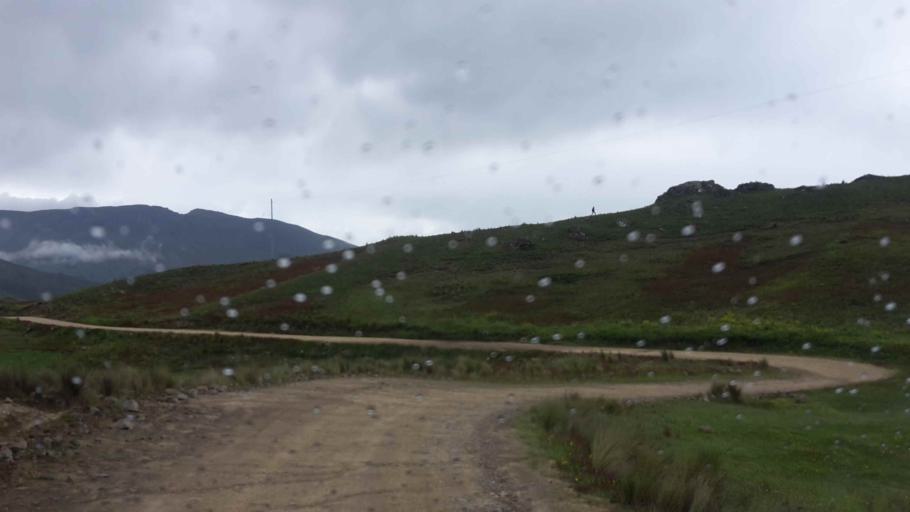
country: BO
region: Cochabamba
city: Cochabamba
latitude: -17.1465
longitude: -66.1020
